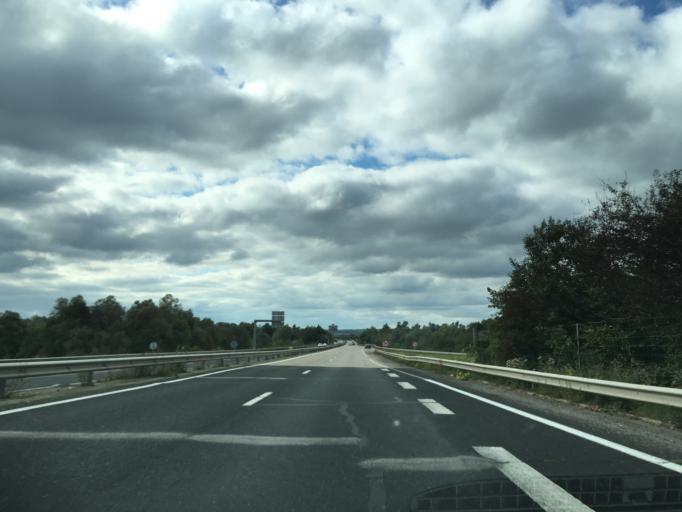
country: FR
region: Lorraine
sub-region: Departement de Meurthe-et-Moselle
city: Chanteheux
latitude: 48.5684
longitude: 6.5341
